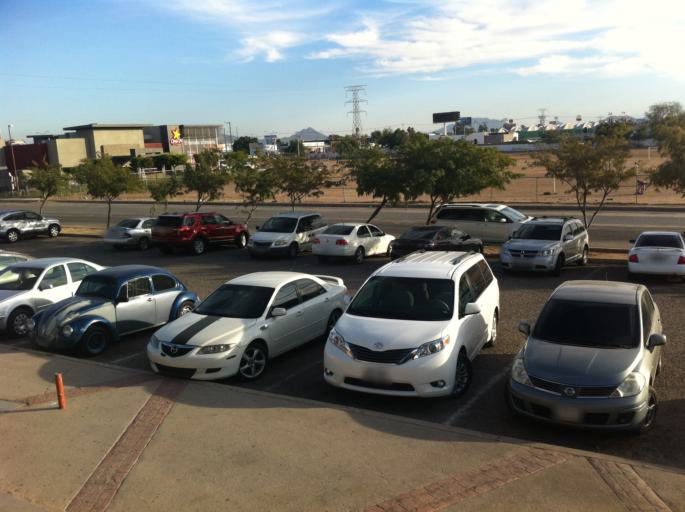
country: MX
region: Sonora
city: Hermosillo
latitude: 29.1062
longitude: -110.9940
